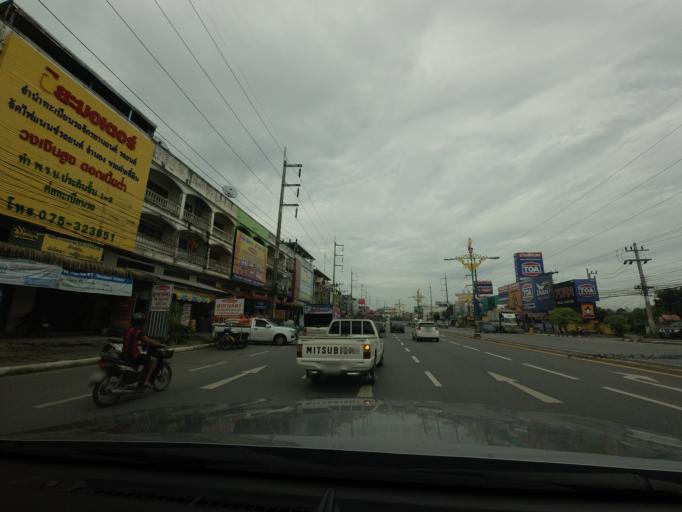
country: TH
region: Nakhon Si Thammarat
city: Nakhon Si Thammarat
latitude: 8.3832
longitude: 99.9774
